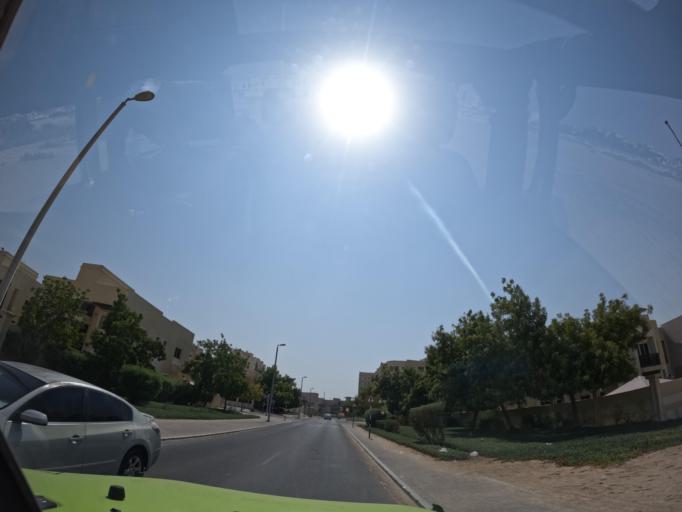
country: AE
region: Abu Dhabi
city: Abu Dhabi
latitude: 24.3149
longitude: 54.6230
